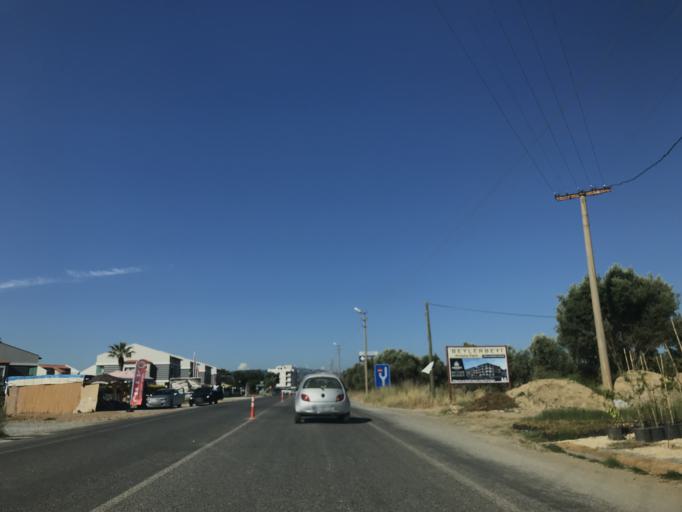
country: TR
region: Aydin
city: Davutlar
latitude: 37.7309
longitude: 27.2716
